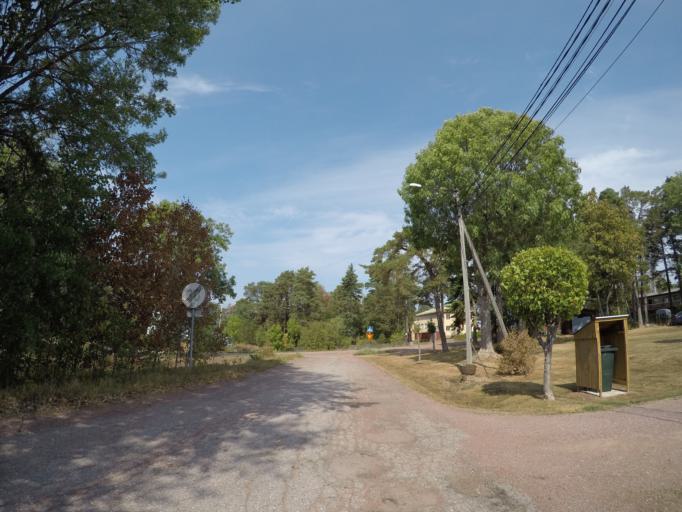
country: AX
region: Alands landsbygd
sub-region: Saltvik
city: Saltvik
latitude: 60.2327
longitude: 19.9995
